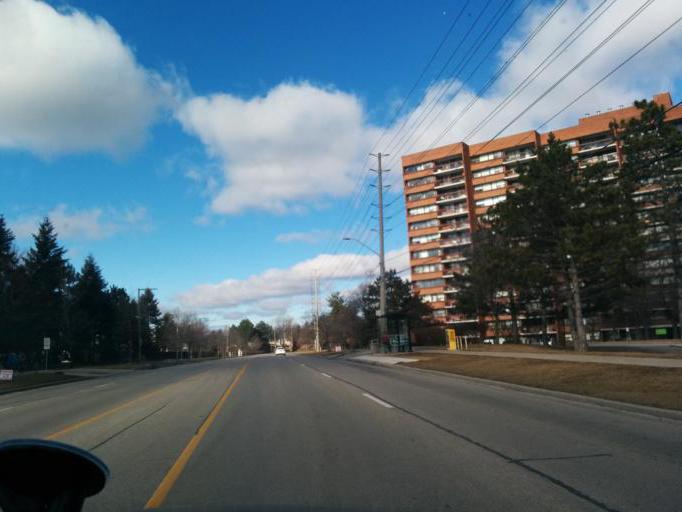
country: CA
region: Ontario
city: Mississauga
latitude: 43.5376
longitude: -79.6870
